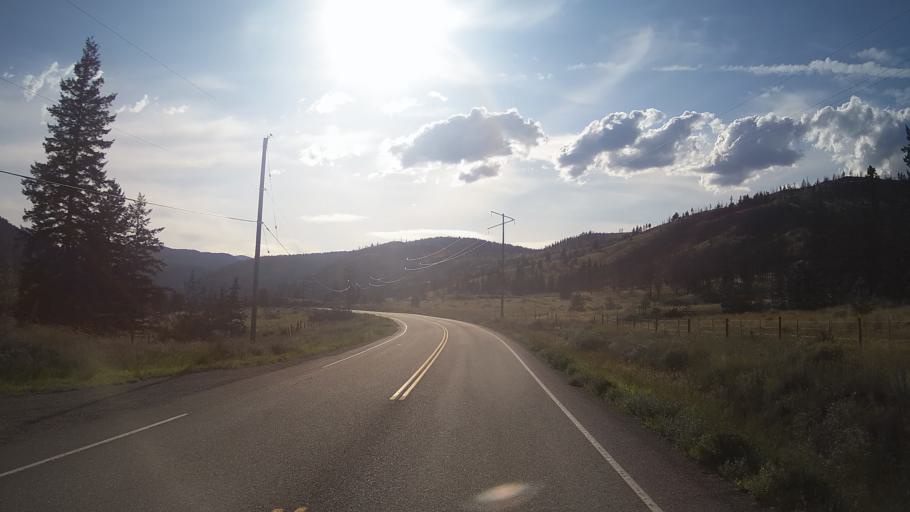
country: CA
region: British Columbia
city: Cache Creek
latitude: 50.8871
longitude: -121.4616
